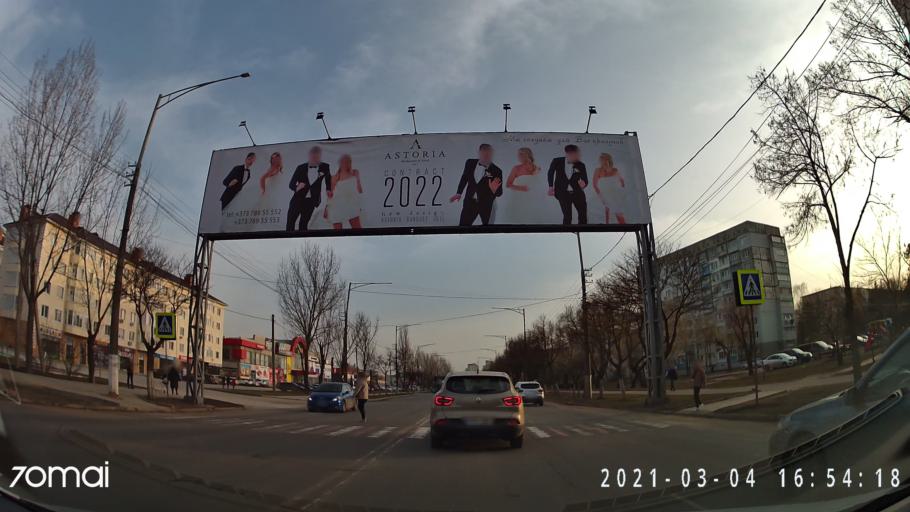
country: MD
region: Balti
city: Balti
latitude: 47.7649
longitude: 27.9414
